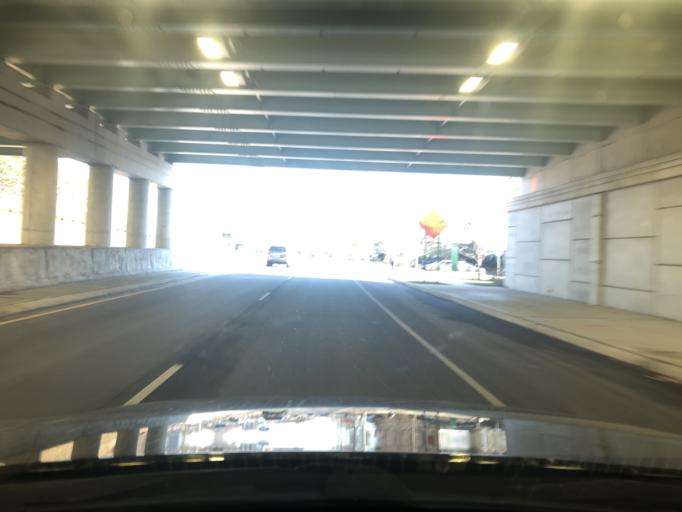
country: US
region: New Jersey
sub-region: Atlantic County
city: Northfield
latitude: 39.4002
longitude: -74.5600
